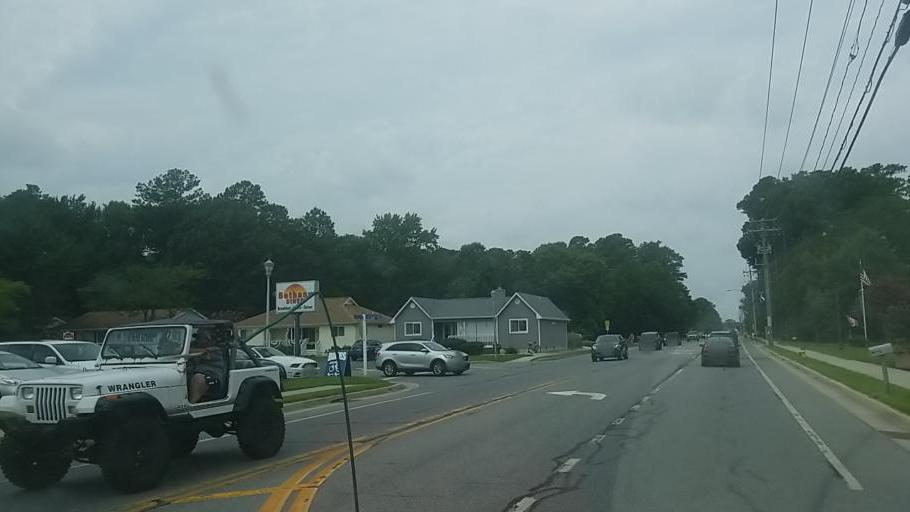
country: US
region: Delaware
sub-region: Sussex County
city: Bethany Beach
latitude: 38.5407
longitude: -75.0724
